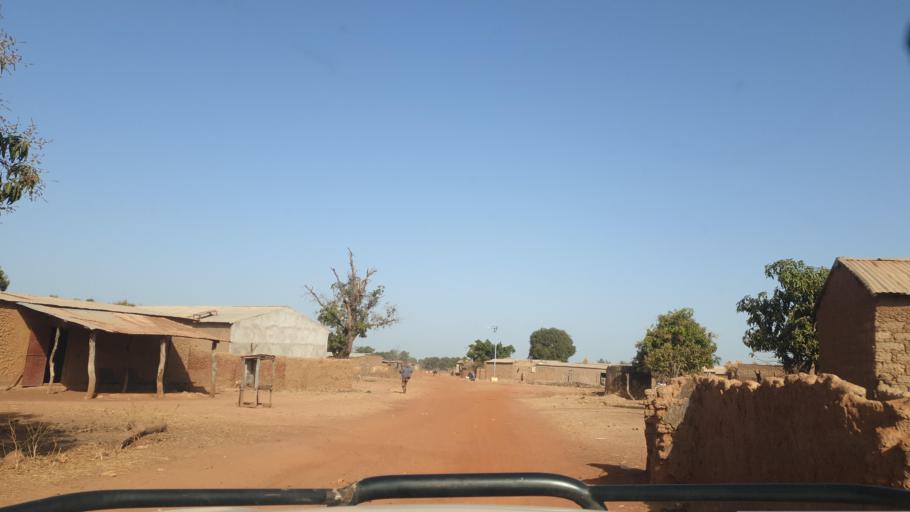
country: ML
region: Sikasso
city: Kolondieba
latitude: 11.7314
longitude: -6.8899
